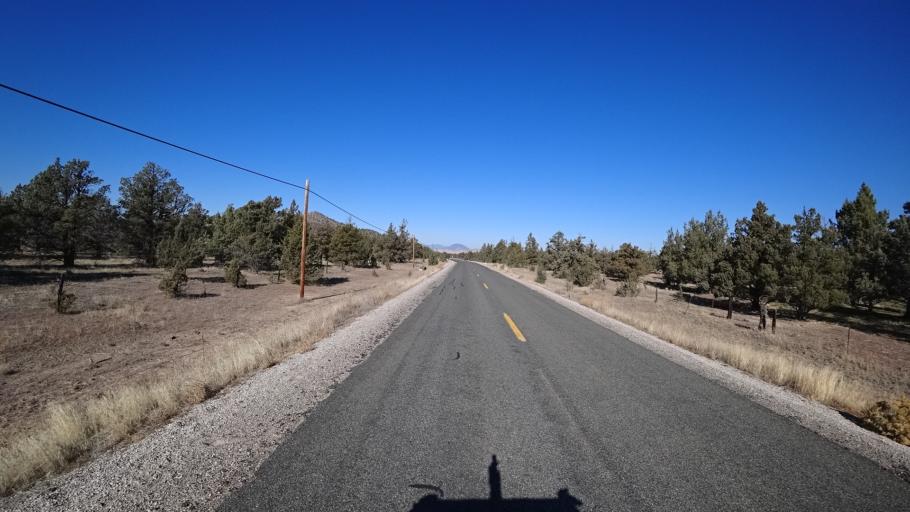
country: US
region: California
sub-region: Siskiyou County
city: Montague
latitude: 41.6578
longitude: -122.3653
